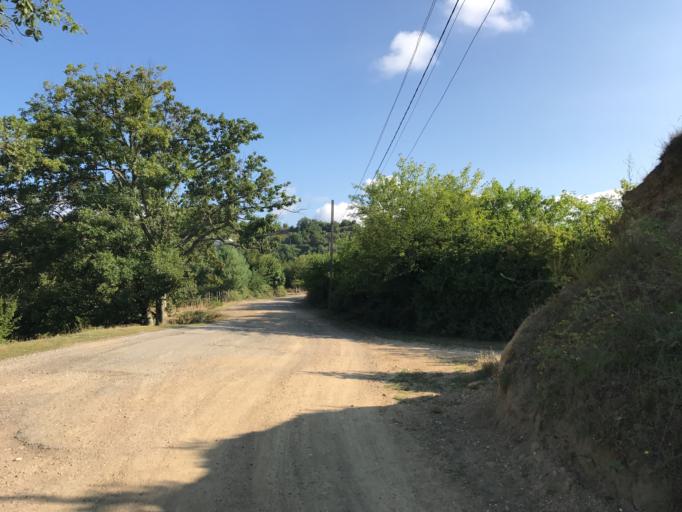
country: GE
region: Abkhazia
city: Bich'vinta
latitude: 43.1787
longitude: 40.3989
